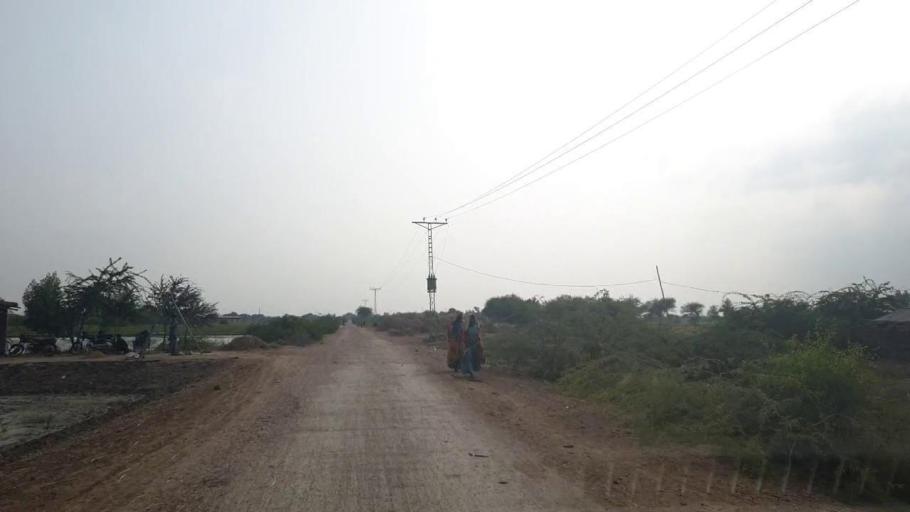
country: PK
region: Sindh
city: Badin
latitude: 24.6215
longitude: 68.6882
